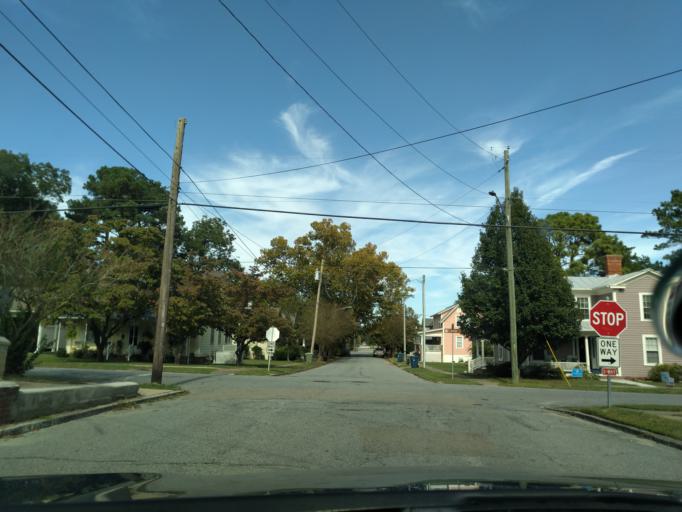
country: US
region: North Carolina
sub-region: Beaufort County
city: Washington
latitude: 35.5391
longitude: -77.0490
